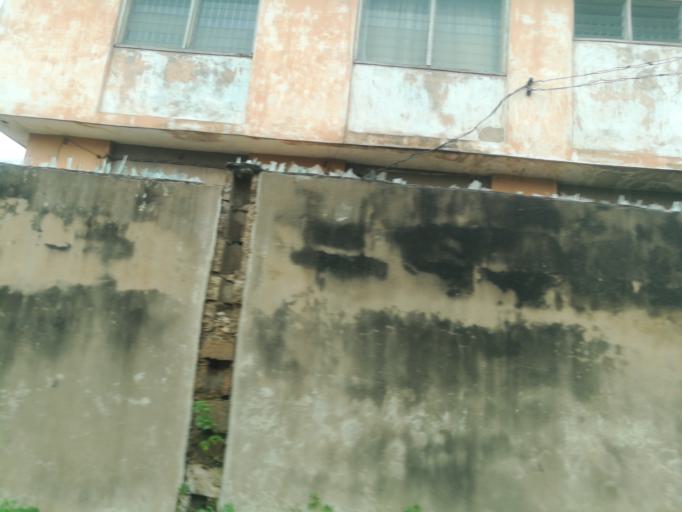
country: NG
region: Oyo
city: Ibadan
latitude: 7.4298
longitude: 3.9238
